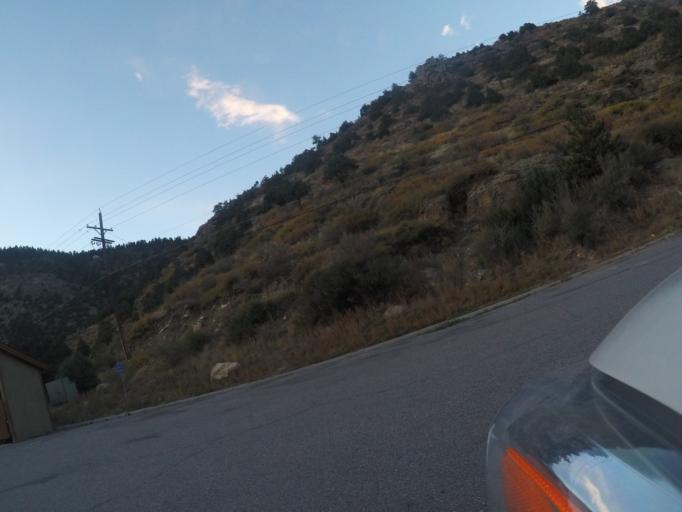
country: US
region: Colorado
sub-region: Clear Creek County
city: Idaho Springs
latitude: 39.7660
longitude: -105.6121
